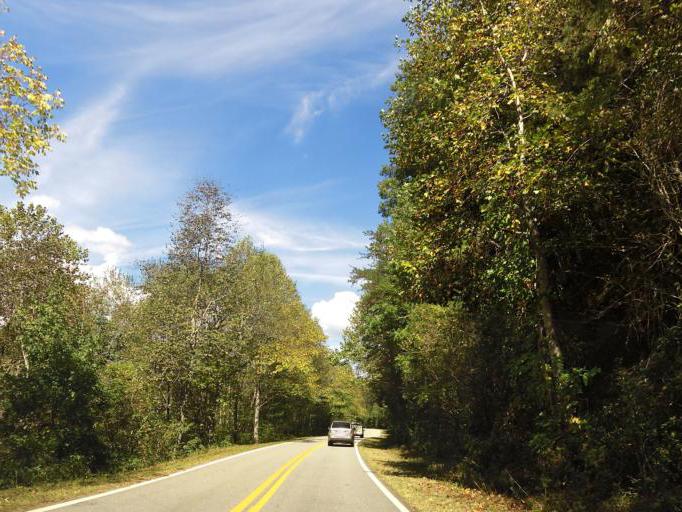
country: US
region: Georgia
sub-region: Pickens County
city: Jasper
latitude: 34.5081
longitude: -84.2777
